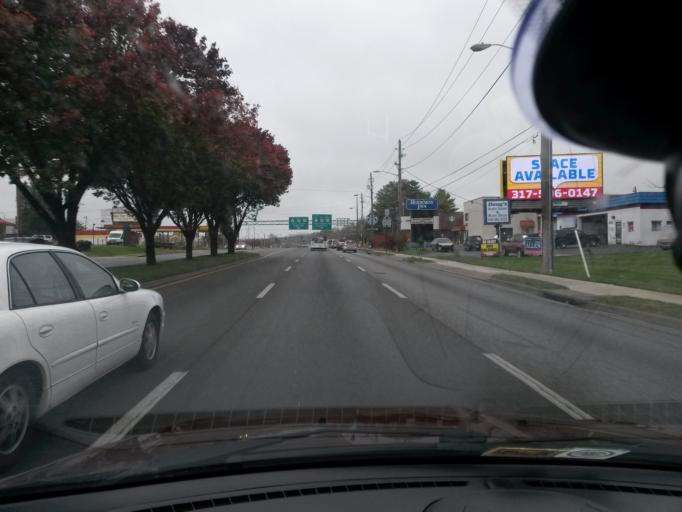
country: US
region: Virginia
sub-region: City of Roanoke
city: Roanoke
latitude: 37.2825
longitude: -79.9309
